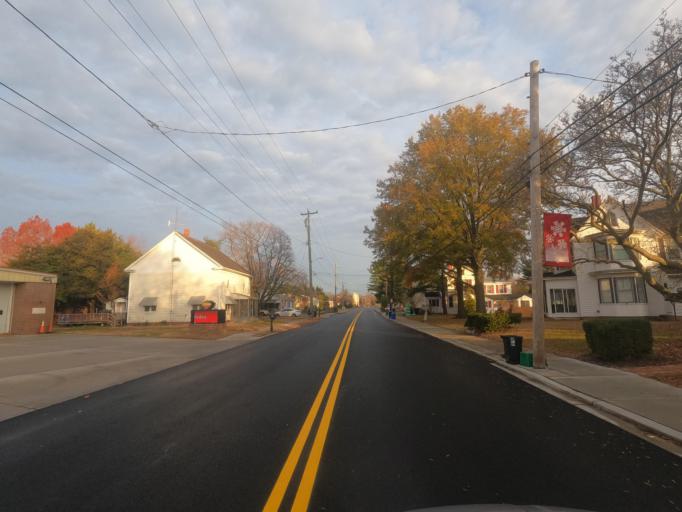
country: US
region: Delaware
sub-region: New Castle County
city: Townsend
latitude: 39.2604
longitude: -75.8371
